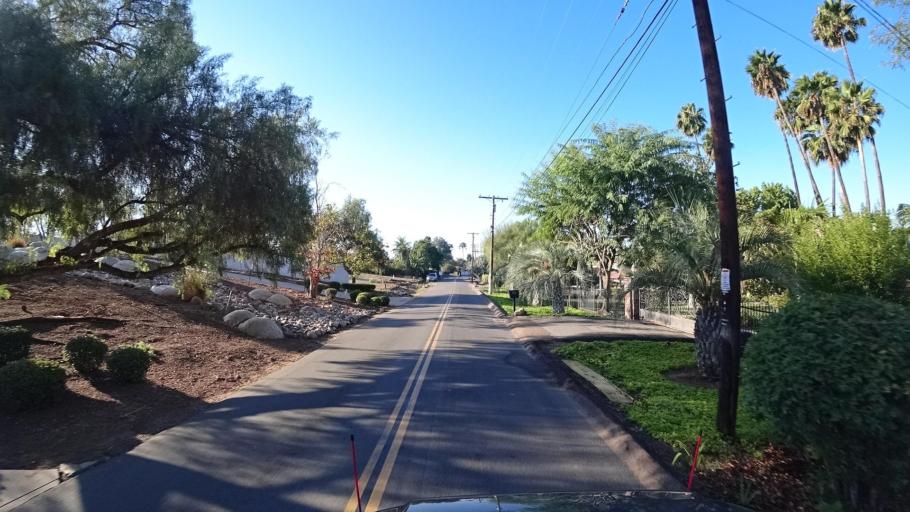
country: US
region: California
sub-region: San Diego County
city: Casa de Oro-Mount Helix
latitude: 32.7674
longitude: -116.9692
